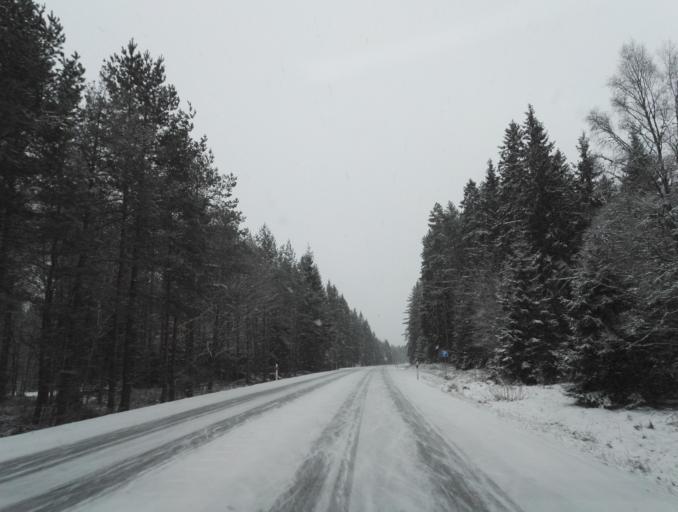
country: SE
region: Kronoberg
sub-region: Uppvidinge Kommun
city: Lenhovda
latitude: 57.0135
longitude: 15.2577
